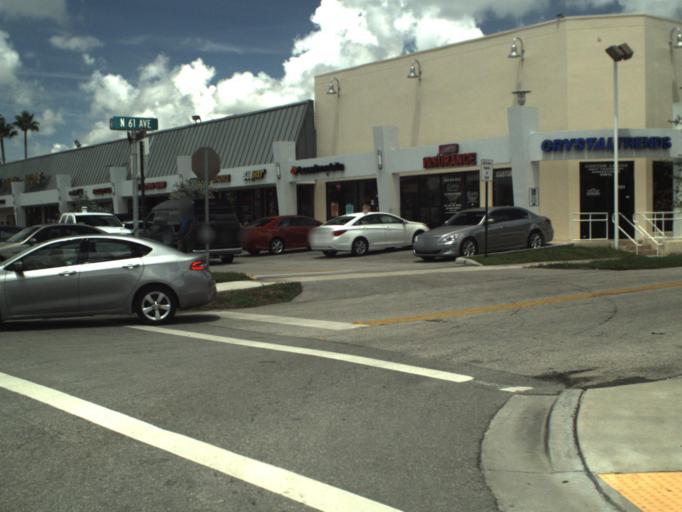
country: US
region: Florida
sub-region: Broward County
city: Pembroke Pines
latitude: 26.0102
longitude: -80.2101
